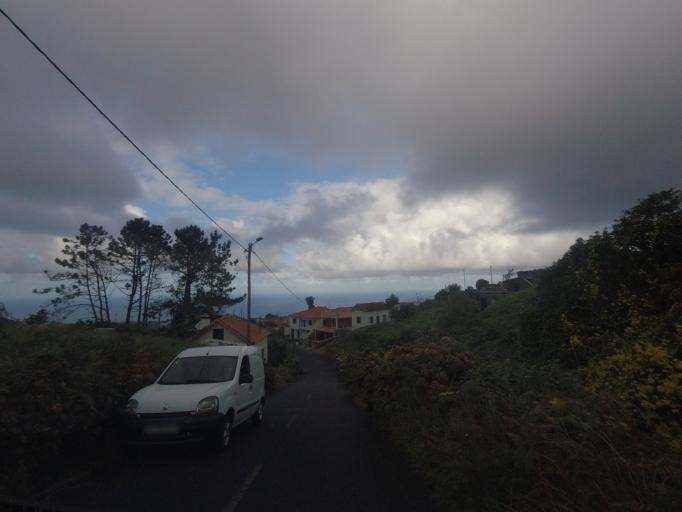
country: PT
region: Madeira
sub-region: Santana
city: Santana
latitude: 32.7994
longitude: -16.8872
